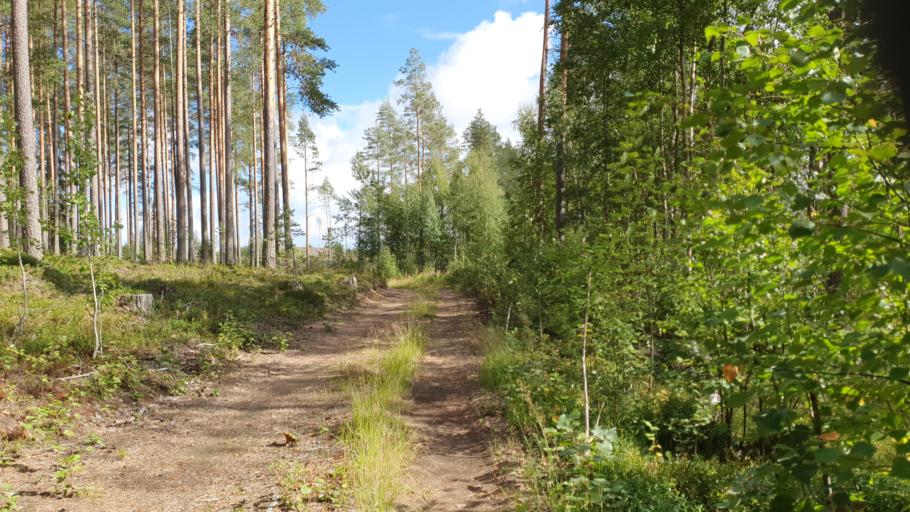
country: FI
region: Kainuu
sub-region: Kehys-Kainuu
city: Kuhmo
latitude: 64.1482
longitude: 29.3485
